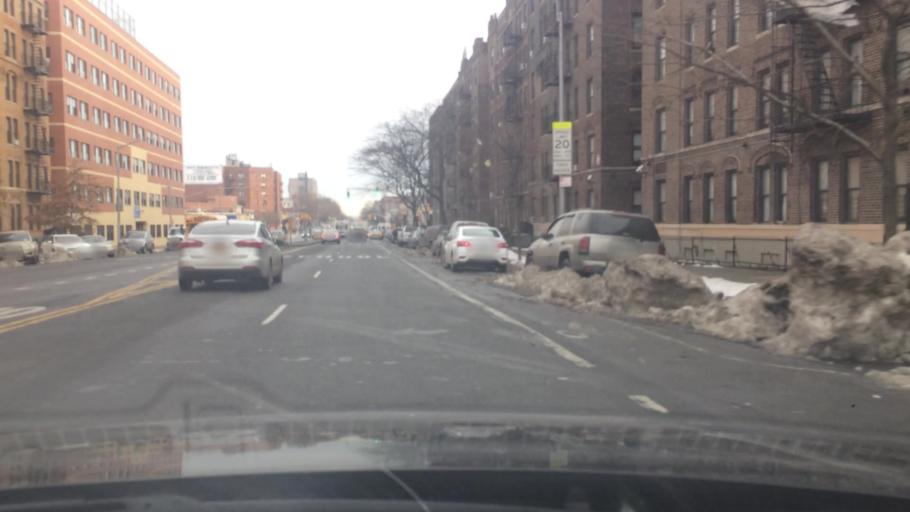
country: US
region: New York
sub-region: Kings County
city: Brooklyn
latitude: 40.6626
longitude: -73.9218
